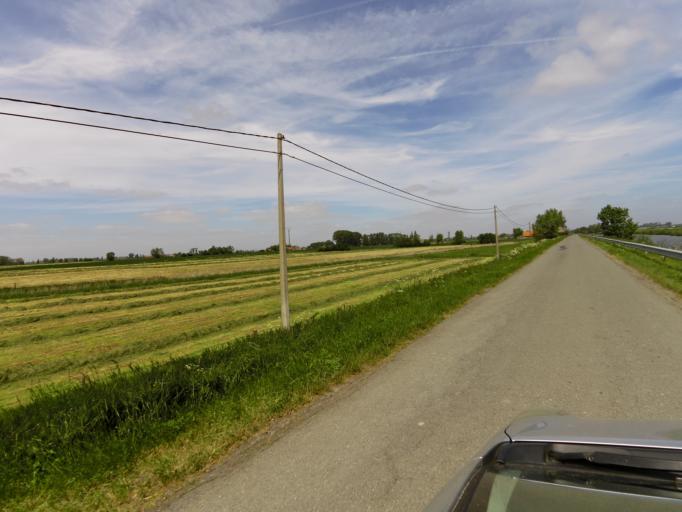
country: BE
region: Flanders
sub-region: Provincie West-Vlaanderen
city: Diksmuide
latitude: 51.0049
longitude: 2.8327
